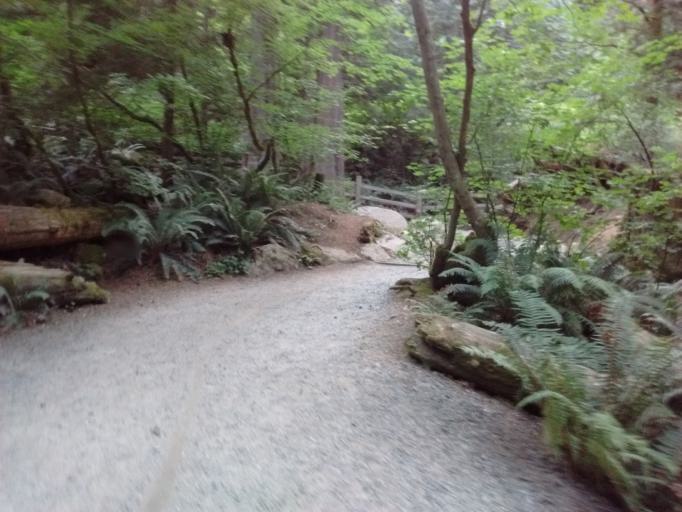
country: CA
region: British Columbia
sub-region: Greater Vancouver Regional District
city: Lions Bay
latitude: 49.6707
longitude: -123.1585
